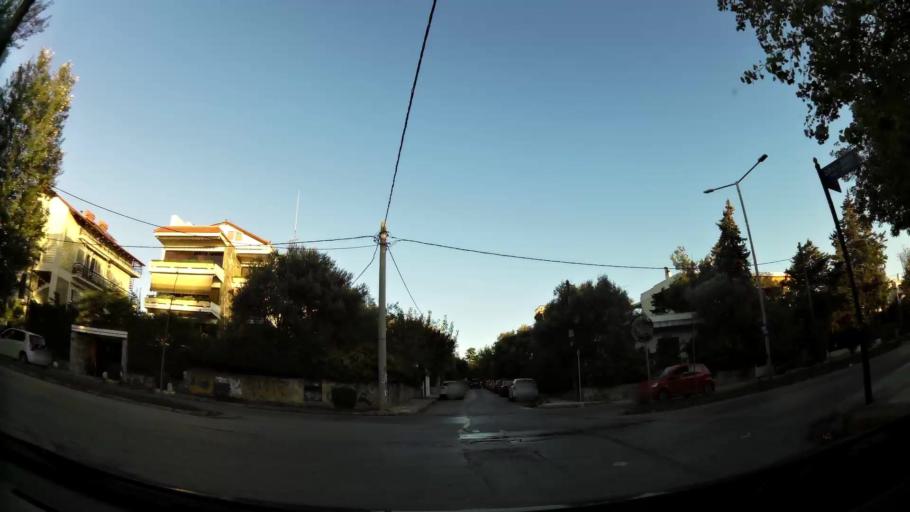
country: GR
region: Attica
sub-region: Nomarchia Athinas
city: Kifisia
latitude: 38.0849
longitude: 23.8186
